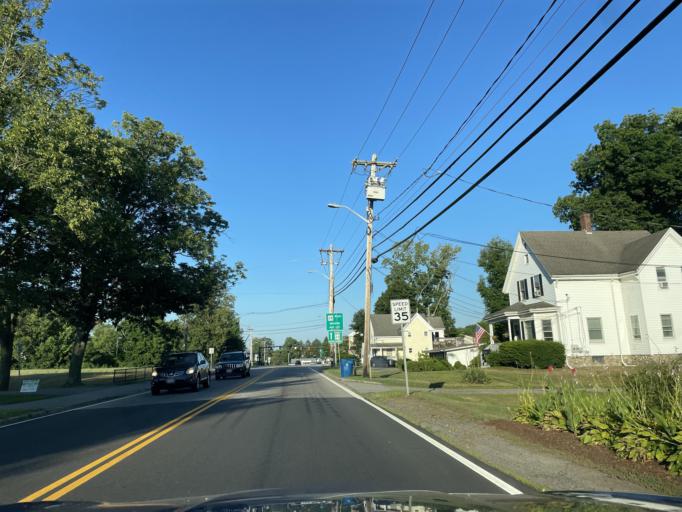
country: US
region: Massachusetts
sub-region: Plymouth County
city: West Bridgewater
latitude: 42.0186
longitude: -71.0106
